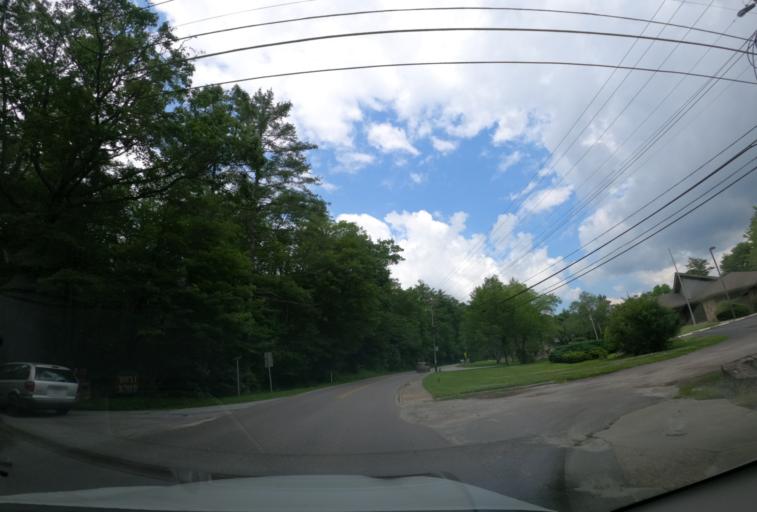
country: US
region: North Carolina
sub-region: Macon County
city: Franklin
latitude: 35.0551
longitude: -83.2041
